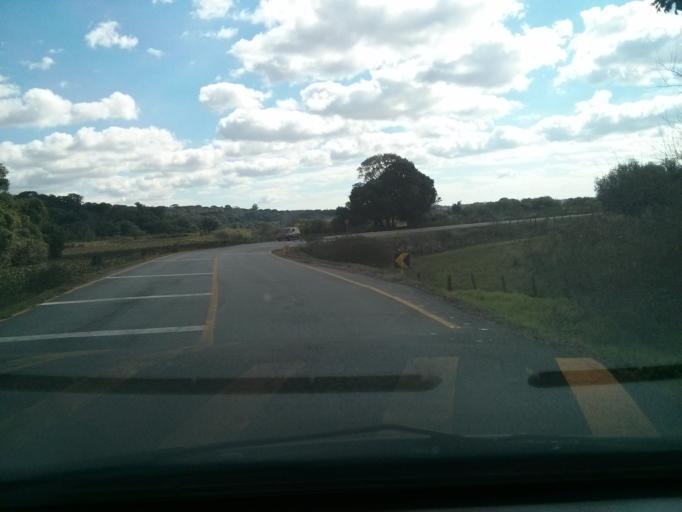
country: BR
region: Parana
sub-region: Sao Jose Dos Pinhais
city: Sao Jose dos Pinhais
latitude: -25.5545
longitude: -49.2263
